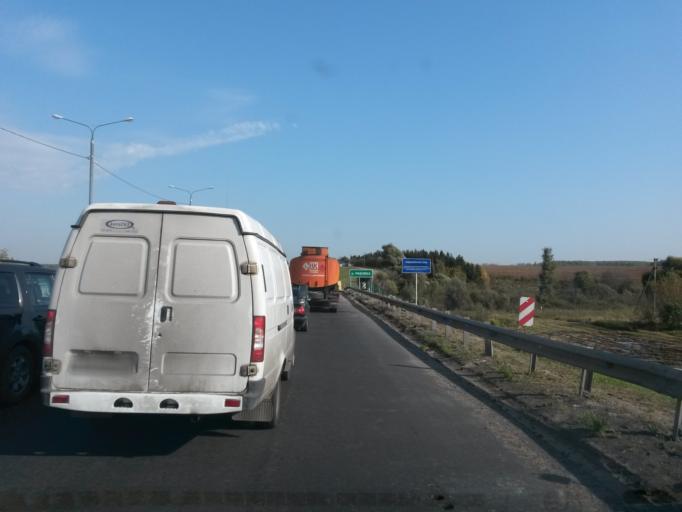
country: RU
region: Moskovskaya
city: Klimovsk
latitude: 55.3471
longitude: 37.5897
